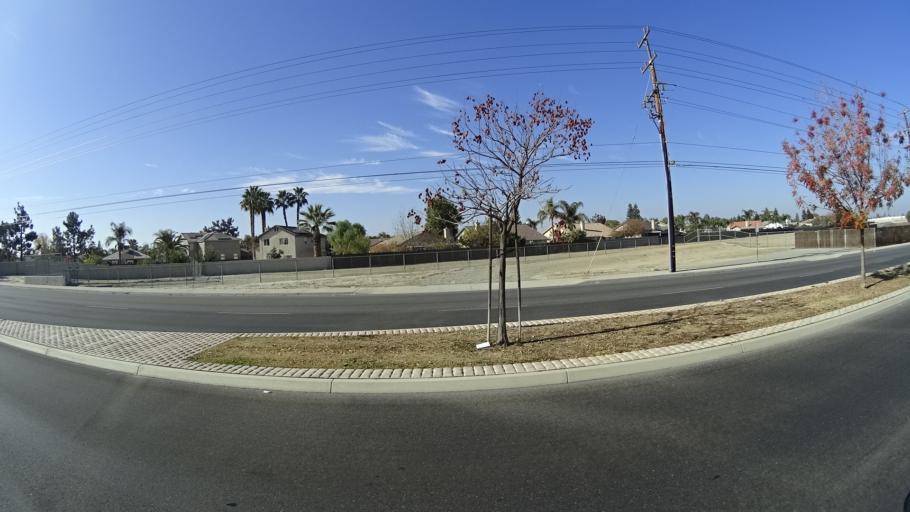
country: US
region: California
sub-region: Kern County
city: Greenfield
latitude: 35.3042
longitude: -119.0743
